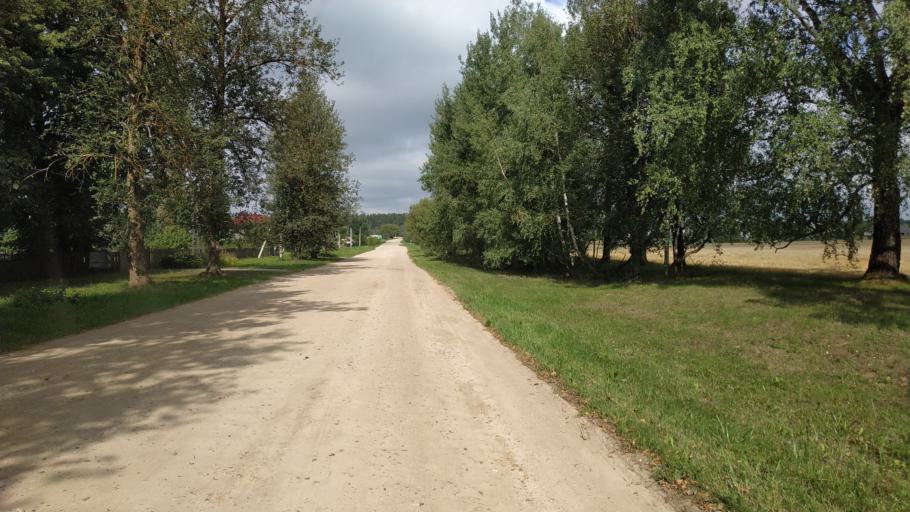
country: BY
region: Mogilev
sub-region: Mahilyowski Rayon
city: Kadino
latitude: 53.8457
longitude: 30.4769
